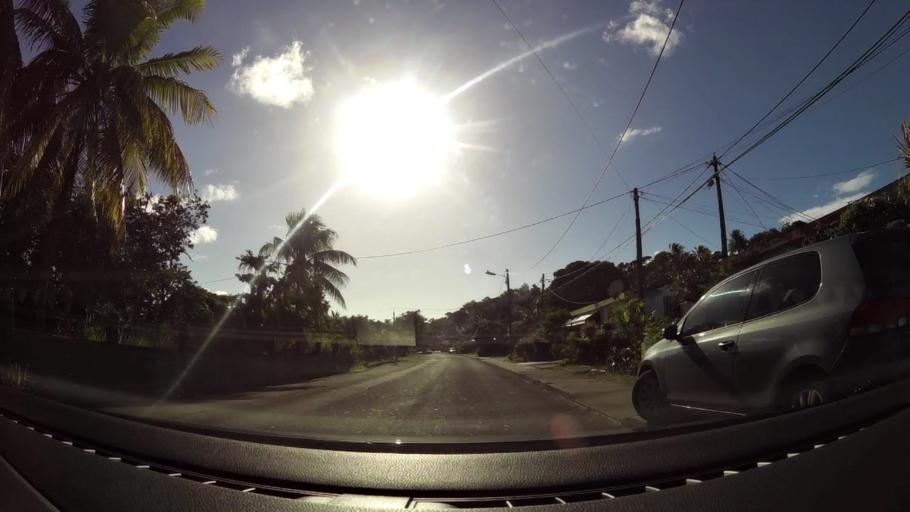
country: GP
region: Guadeloupe
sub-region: Guadeloupe
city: Petit-Canal
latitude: 16.3271
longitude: -61.4481
